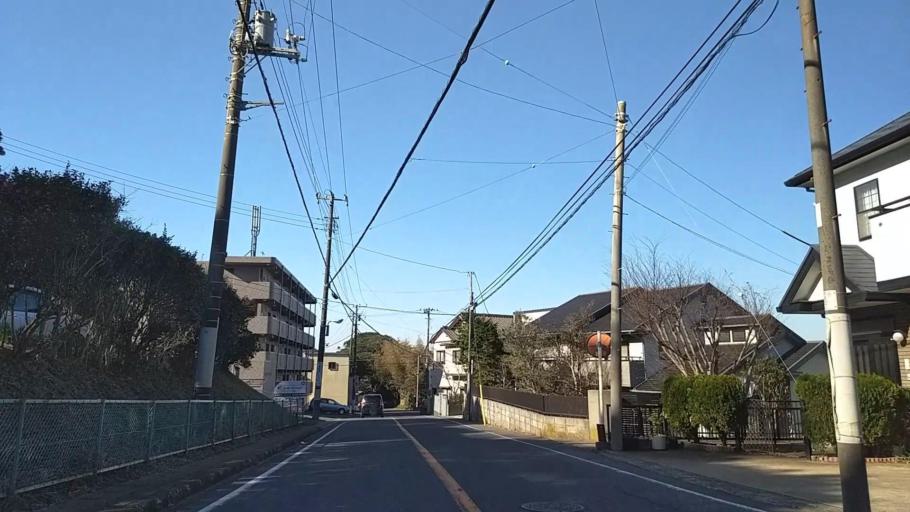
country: JP
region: Chiba
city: Hasaki
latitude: 35.7328
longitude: 140.8503
